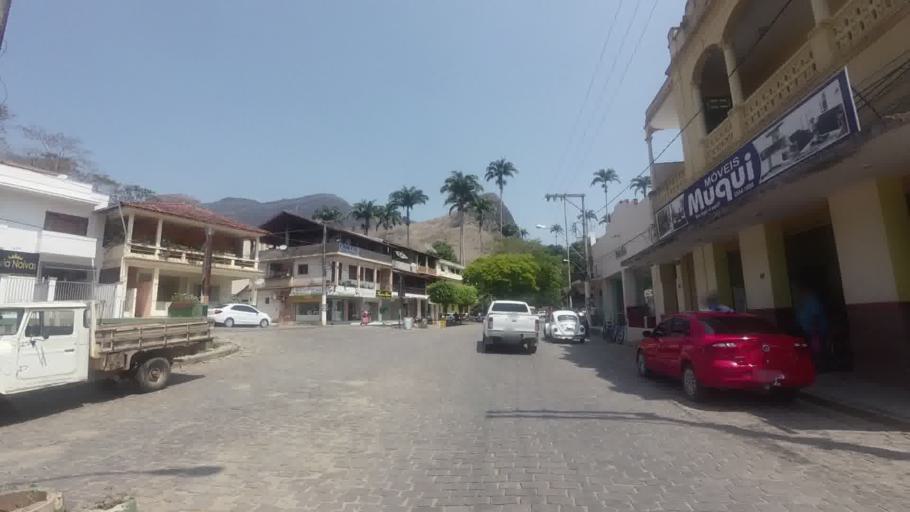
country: BR
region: Espirito Santo
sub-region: Mimoso Do Sul
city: Mimoso do Sul
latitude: -20.9533
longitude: -41.3477
